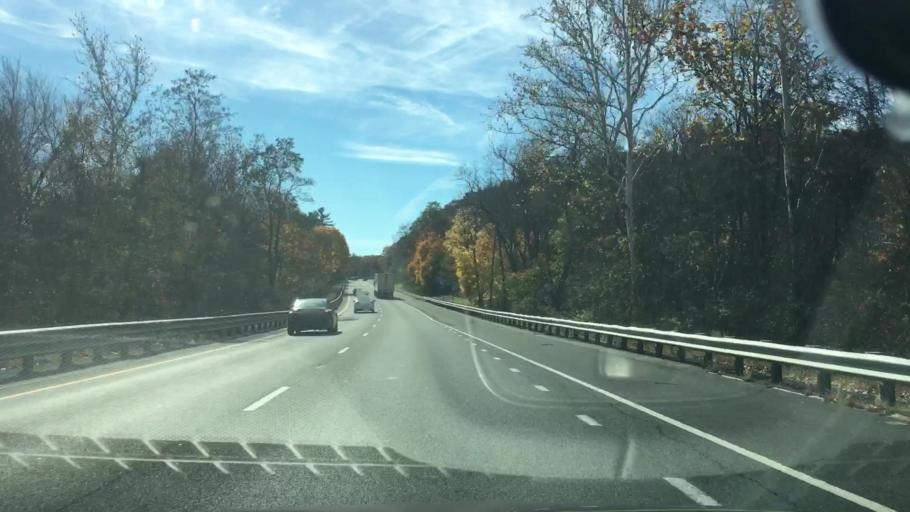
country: US
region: Massachusetts
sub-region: Hampden County
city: Holyoke
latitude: 42.2514
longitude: -72.6231
